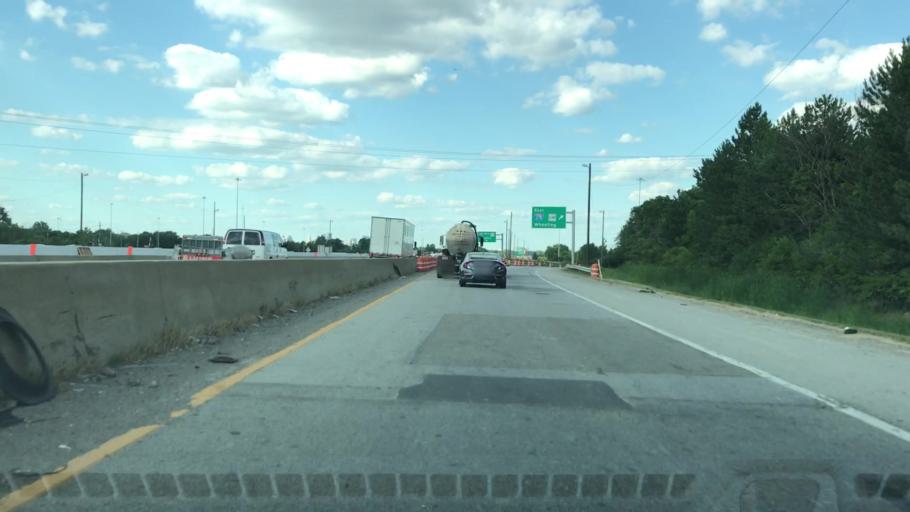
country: US
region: Ohio
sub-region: Franklin County
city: Grove City
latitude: 39.8871
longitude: -83.0432
